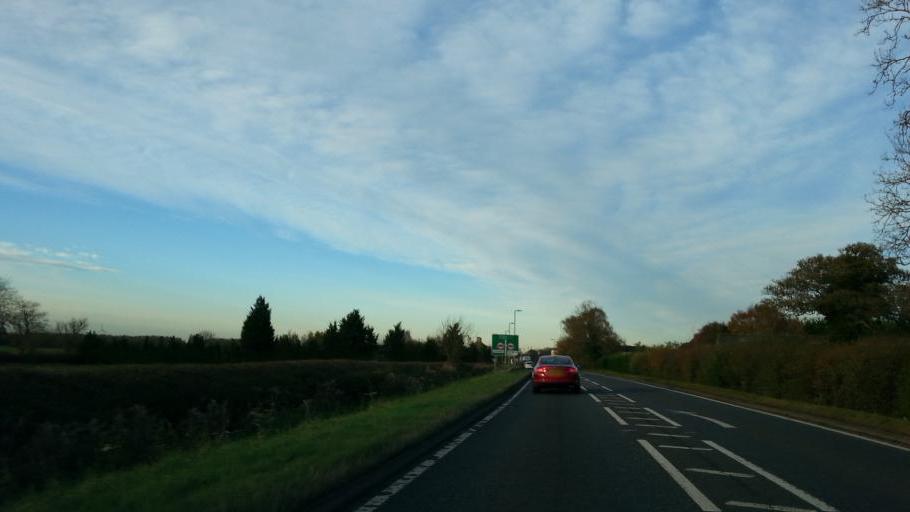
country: GB
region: England
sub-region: Northamptonshire
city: Broughton
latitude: 52.3369
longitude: -0.7866
